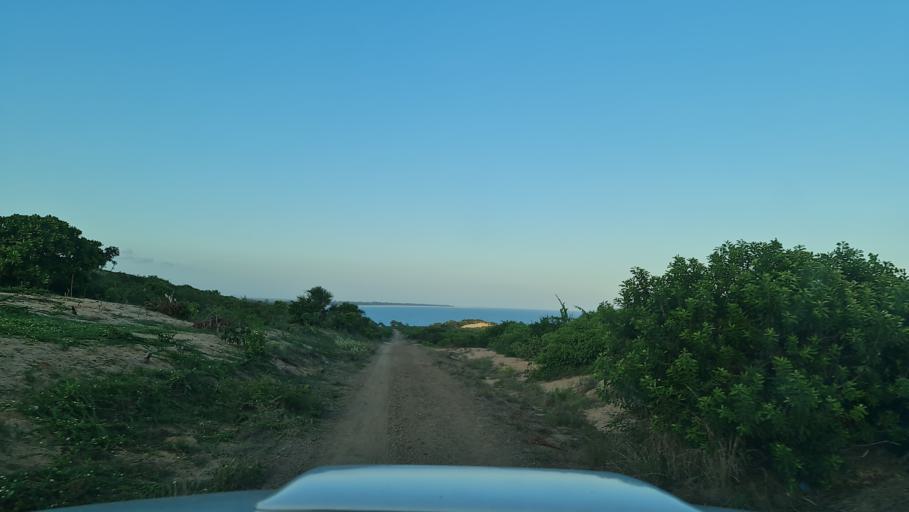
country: MZ
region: Nampula
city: Ilha de Mocambique
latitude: -15.6328
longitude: 40.4182
